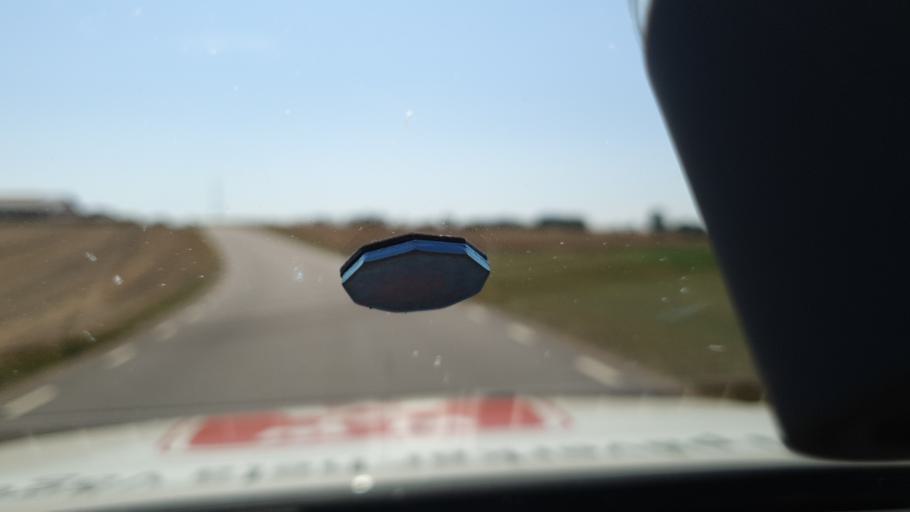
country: SE
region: Skane
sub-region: Sjobo Kommun
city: Blentarp
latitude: 55.5523
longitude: 13.5597
